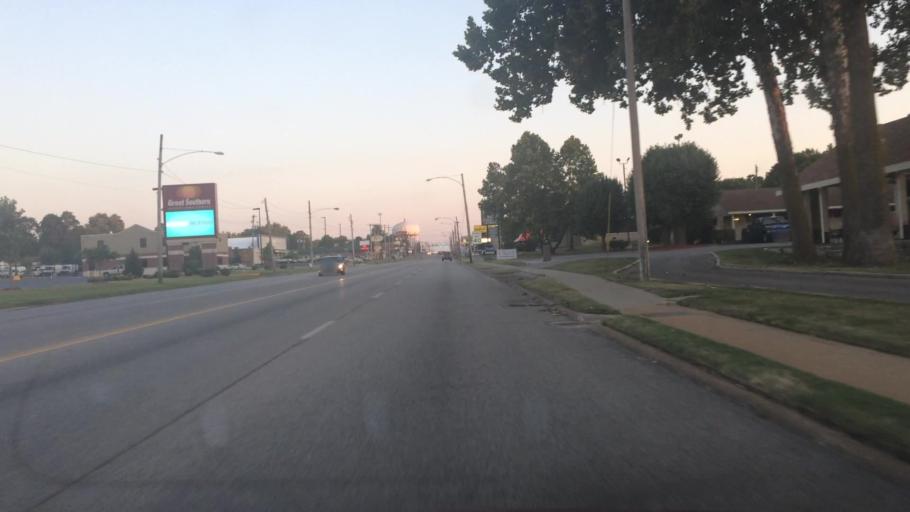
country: US
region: Missouri
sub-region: Greene County
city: Springfield
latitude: 37.2088
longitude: -93.2619
